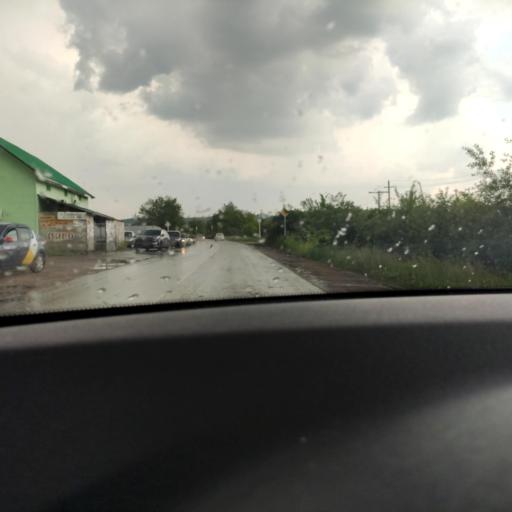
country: RU
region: Samara
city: Novosemeykino
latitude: 53.4039
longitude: 50.3169
